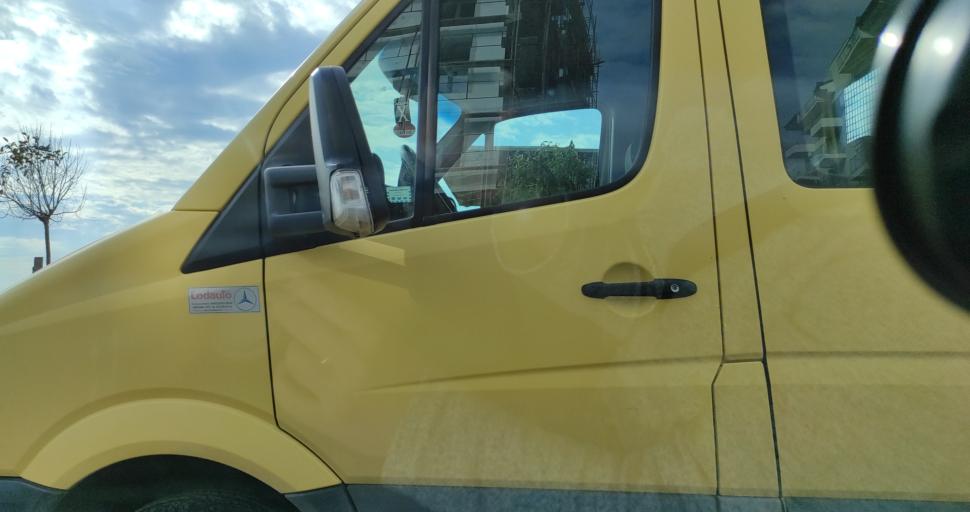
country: AL
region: Lezhe
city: Shengjin
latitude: 41.7955
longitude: 19.6019
